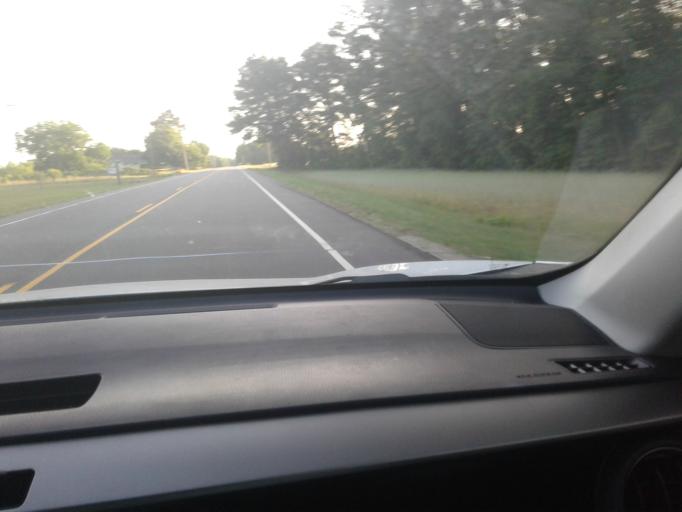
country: US
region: North Carolina
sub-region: Wake County
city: Fuquay-Varina
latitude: 35.5215
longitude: -78.8128
